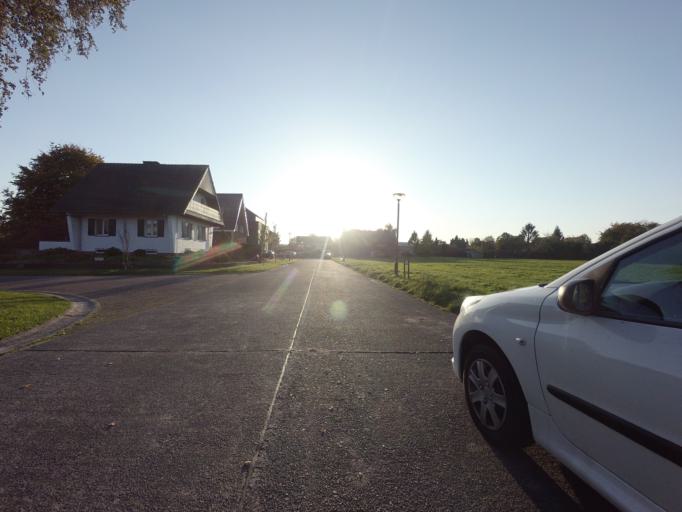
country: BE
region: Flanders
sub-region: Provincie Antwerpen
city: Lint
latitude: 51.1318
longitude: 4.4843
